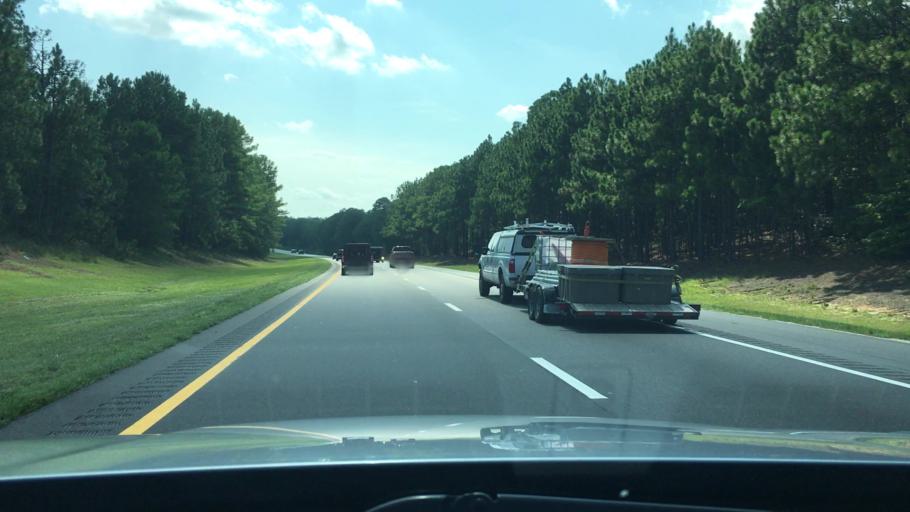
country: US
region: North Carolina
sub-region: Cumberland County
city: Hope Mills
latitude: 34.9697
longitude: -78.8766
